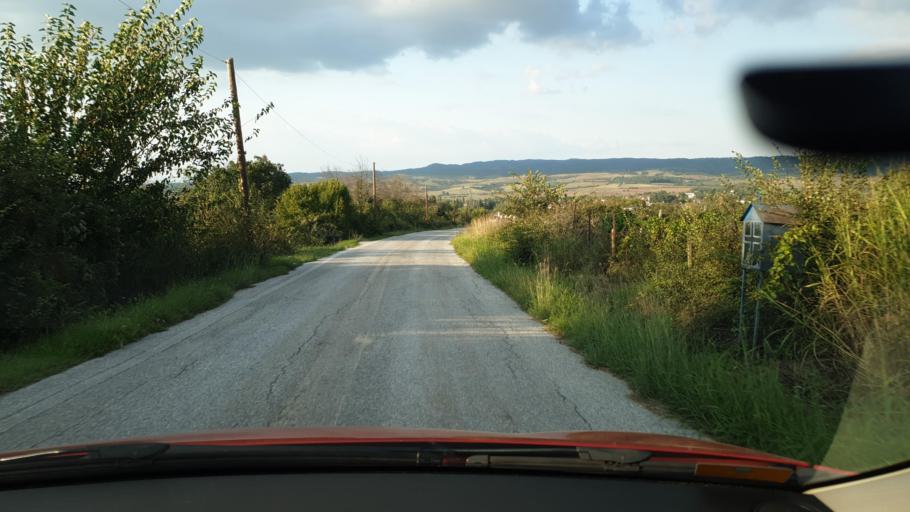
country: GR
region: Central Macedonia
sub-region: Nomos Chalkidikis
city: Galatista
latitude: 40.5606
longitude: 23.2814
